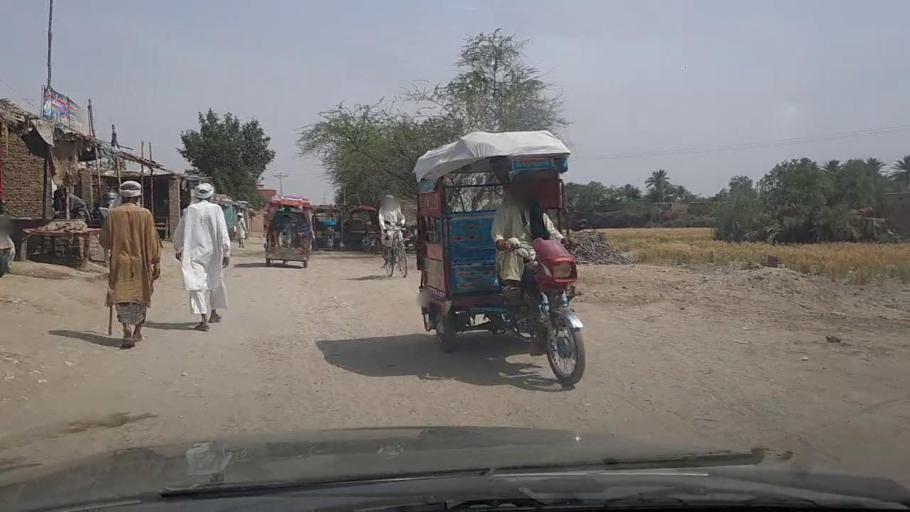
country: PK
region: Sindh
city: Shikarpur
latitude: 27.9281
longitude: 68.6636
